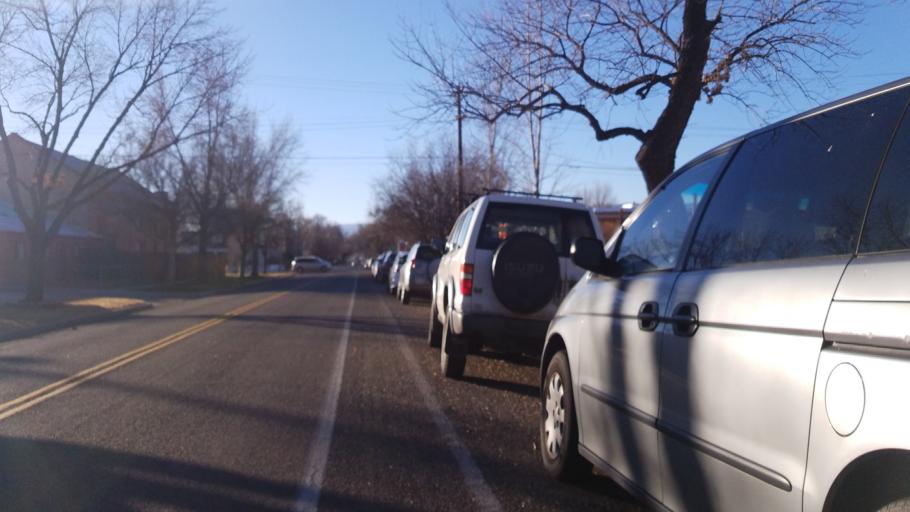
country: US
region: Colorado
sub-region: Mesa County
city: Grand Junction
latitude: 39.0713
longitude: -108.5560
